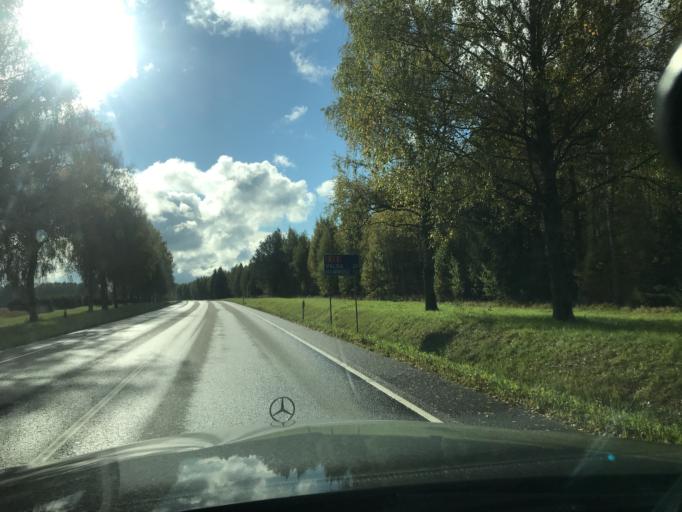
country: EE
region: Valgamaa
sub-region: Torva linn
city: Torva
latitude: 57.9884
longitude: 25.9408
